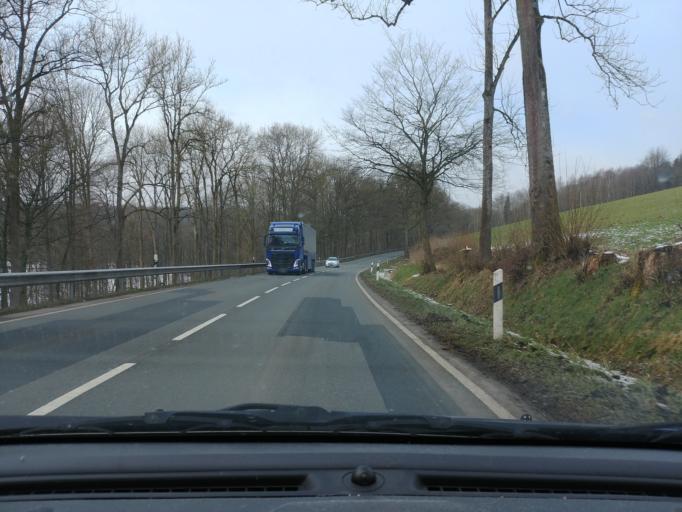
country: DE
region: Lower Saxony
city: Bodenfelde
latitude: 51.6845
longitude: 9.5088
